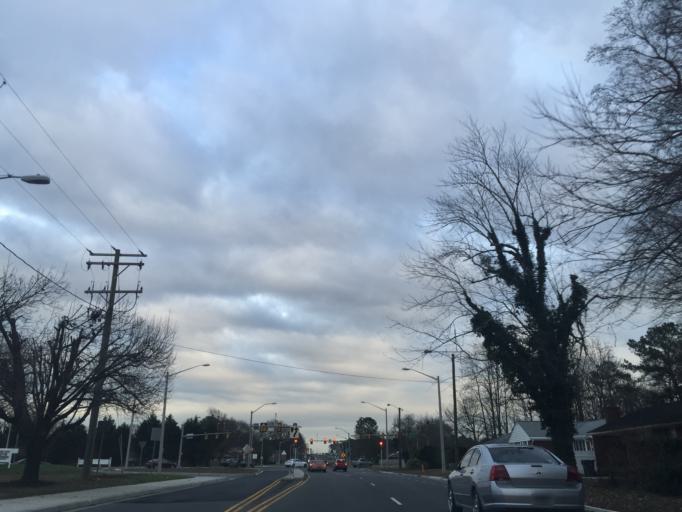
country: US
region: Virginia
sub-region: City of Newport News
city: Newport News
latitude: 37.0878
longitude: -76.5017
